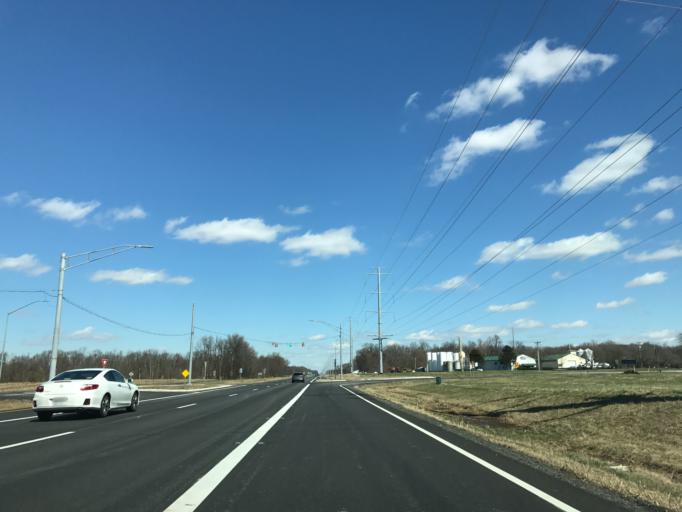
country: US
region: Maryland
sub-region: Queen Anne's County
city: Centreville
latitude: 39.0462
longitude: -76.0086
